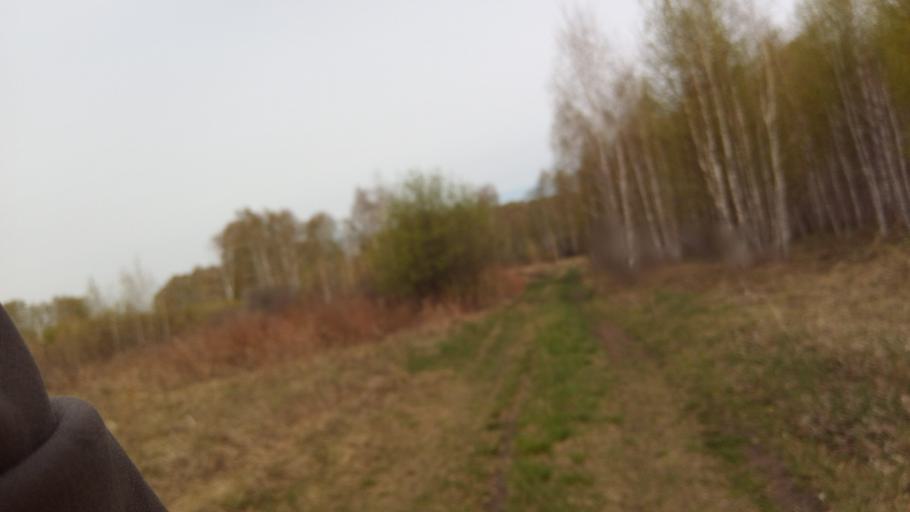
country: RU
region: Chelyabinsk
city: Timiryazevskiy
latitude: 54.9971
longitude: 60.8512
